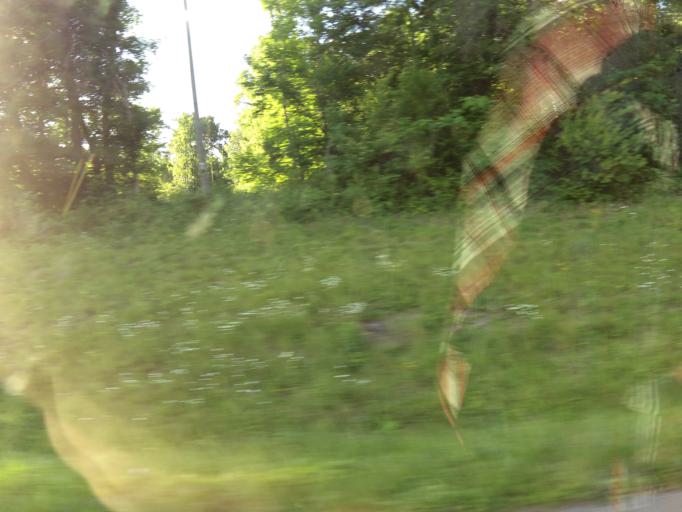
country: US
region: Tennessee
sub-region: Knox County
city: Knoxville
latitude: 35.9006
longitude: -83.8601
